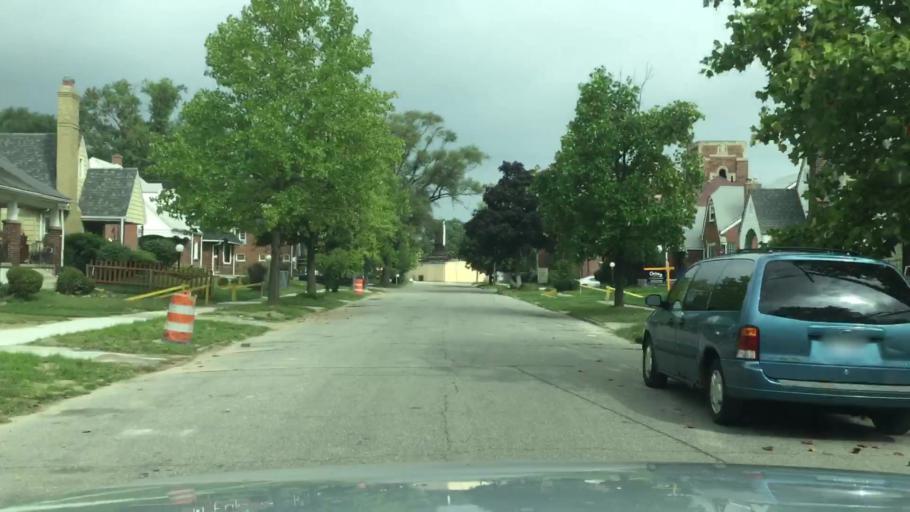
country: US
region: Michigan
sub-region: Oakland County
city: Oak Park
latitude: 42.4052
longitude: -83.1631
